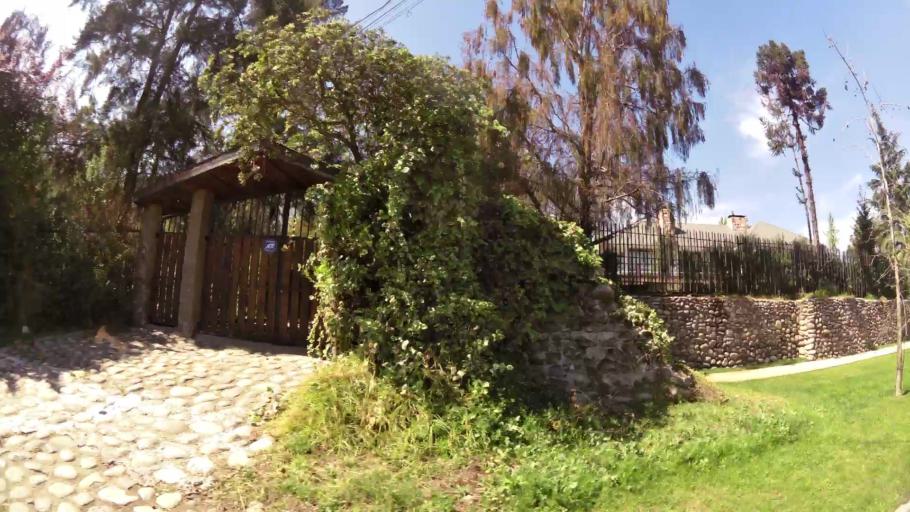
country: CL
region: Santiago Metropolitan
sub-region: Provincia de Santiago
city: Villa Presidente Frei, Nunoa, Santiago, Chile
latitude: -33.4454
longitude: -70.5194
